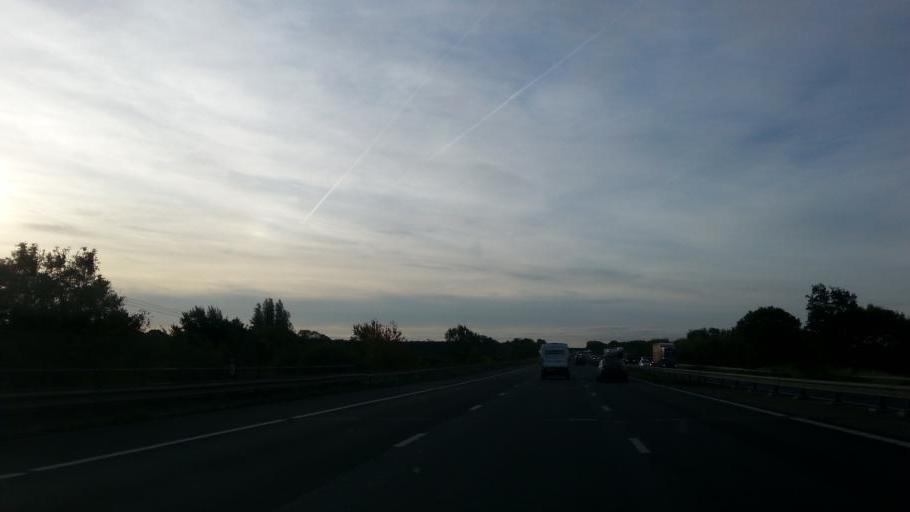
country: GB
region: England
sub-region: Leicestershire
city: Narborough
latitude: 52.5713
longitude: -1.1933
